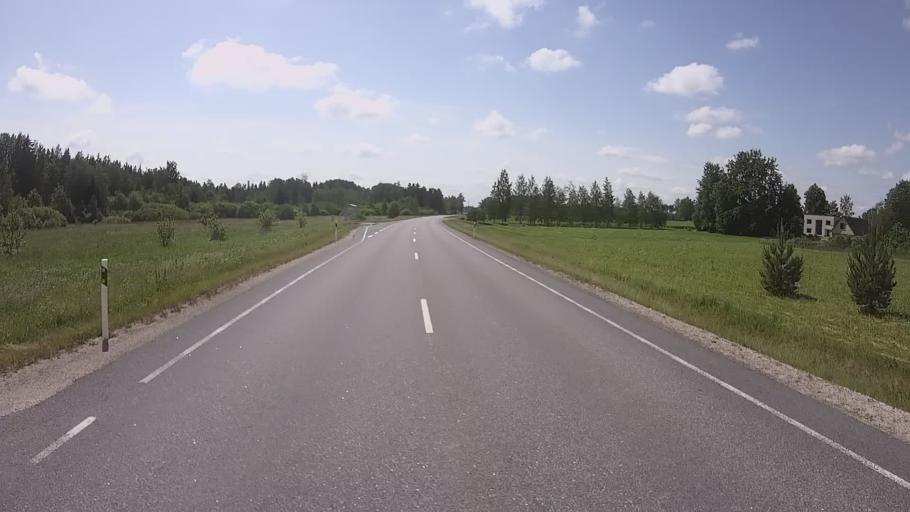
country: EE
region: Tartu
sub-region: Tartu linn
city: Tartu
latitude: 58.3992
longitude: 26.8964
